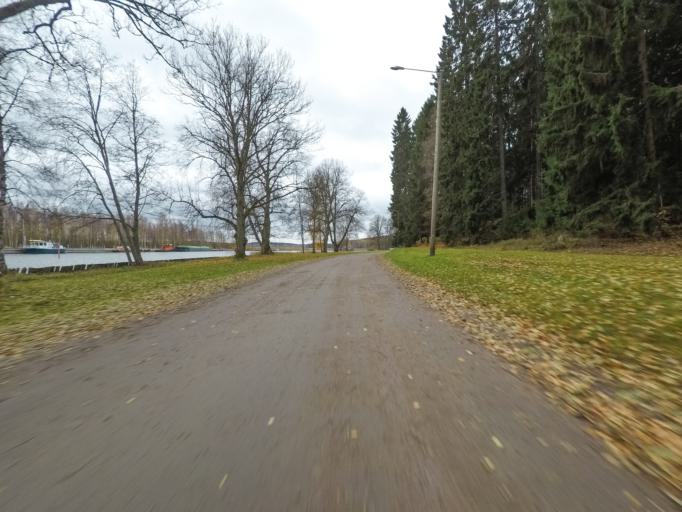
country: FI
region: Uusimaa
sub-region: Porvoo
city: Porvoo
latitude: 60.3794
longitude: 25.6735
